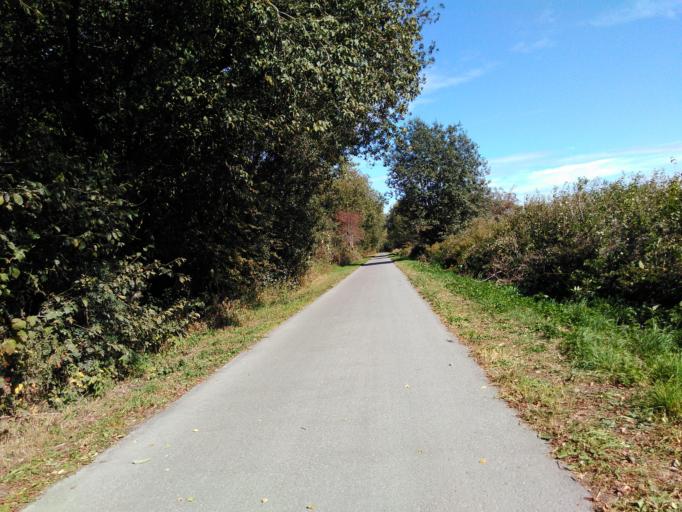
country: BE
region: Wallonia
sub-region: Province du Luxembourg
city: Bastogne
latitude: 50.0171
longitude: 5.7401
